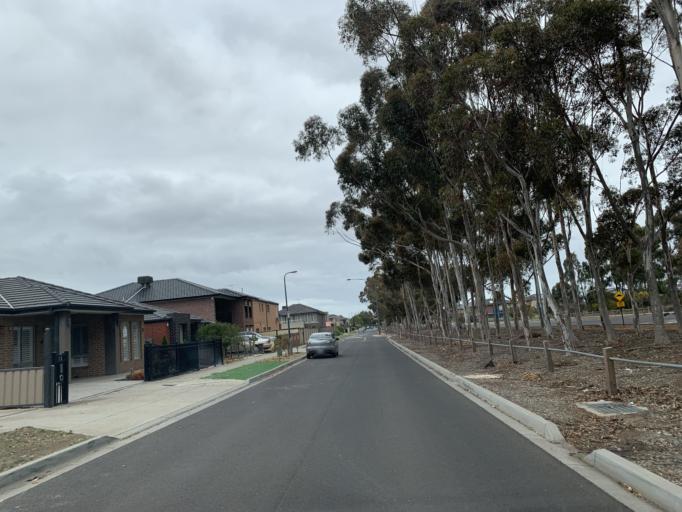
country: AU
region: Victoria
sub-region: Brimbank
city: St Albans
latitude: -37.7555
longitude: 144.8001
